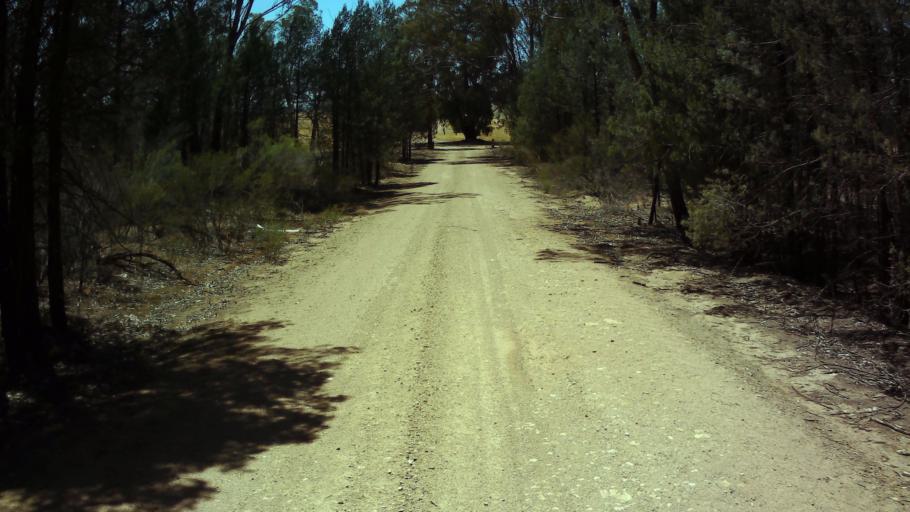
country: AU
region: New South Wales
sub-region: Weddin
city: Grenfell
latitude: -33.7001
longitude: 148.2096
